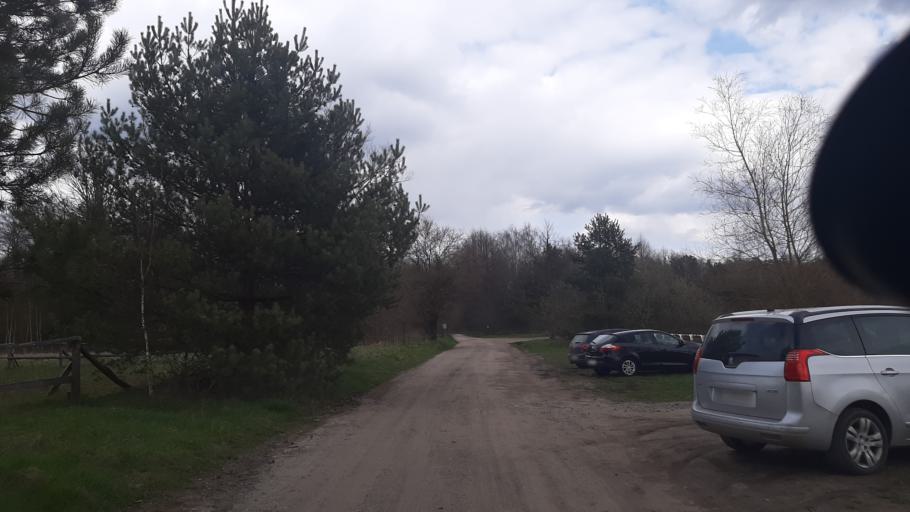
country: PL
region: Lublin Voivodeship
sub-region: Powiat lubelski
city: Niemce
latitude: 51.3863
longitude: 22.5632
